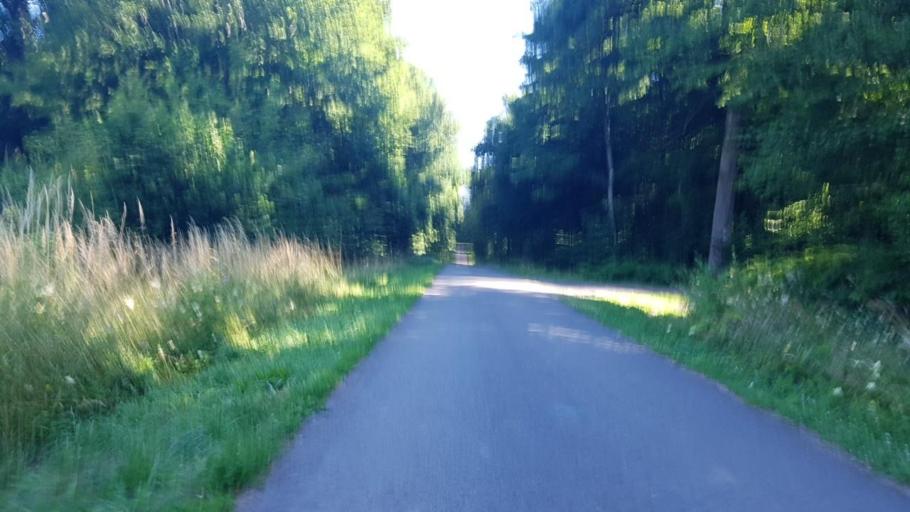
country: FR
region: Nord-Pas-de-Calais
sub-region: Departement du Nord
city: Anor
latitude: 49.9652
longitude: 4.1140
